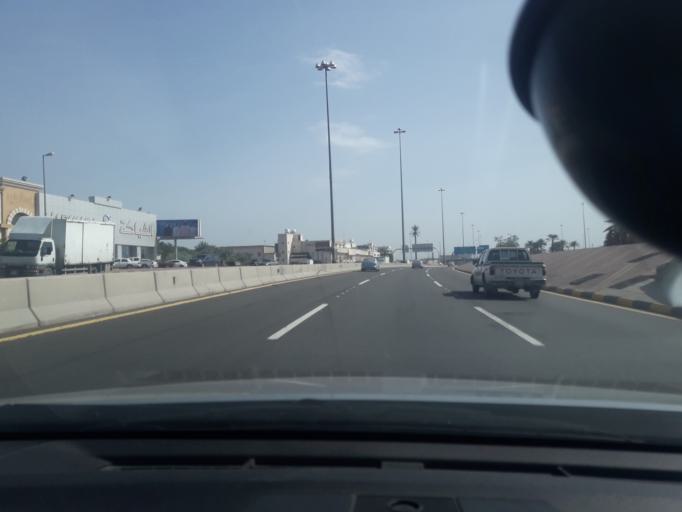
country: SA
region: Al Madinah al Munawwarah
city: Medina
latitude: 24.4408
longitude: 39.6205
